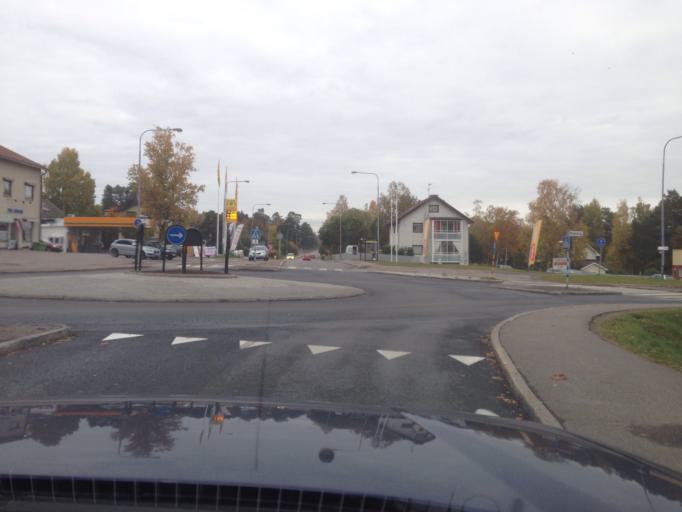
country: SE
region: Vaesternorrland
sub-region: Sundsvalls Kommun
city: Sundsvall
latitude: 62.4006
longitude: 17.3276
